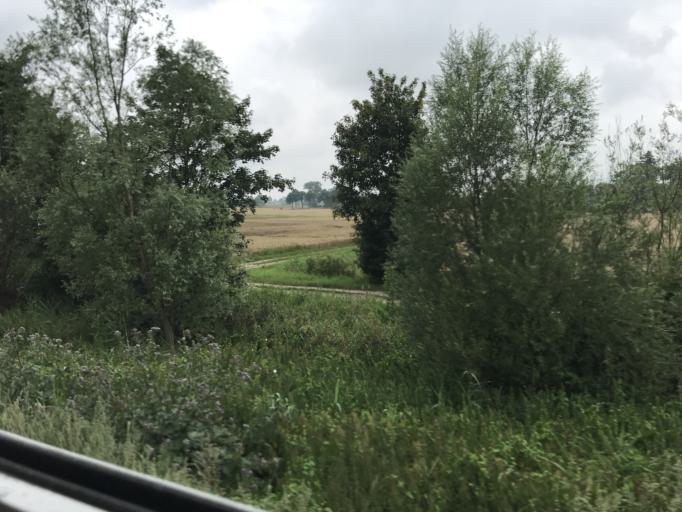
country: PL
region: Warmian-Masurian Voivodeship
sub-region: Powiat elblaski
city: Gronowo Elblaskie
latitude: 54.0977
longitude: 19.3232
